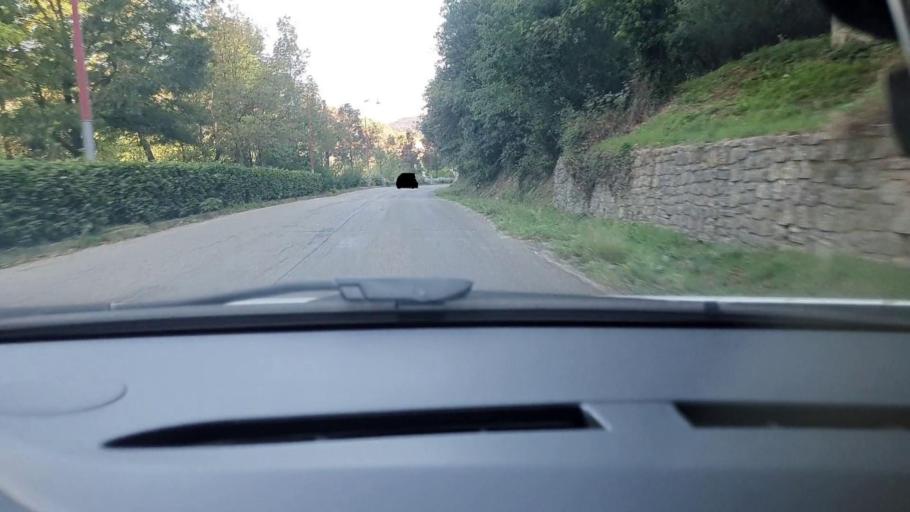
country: FR
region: Languedoc-Roussillon
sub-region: Departement du Gard
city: Besseges
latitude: 44.2952
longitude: 4.0936
